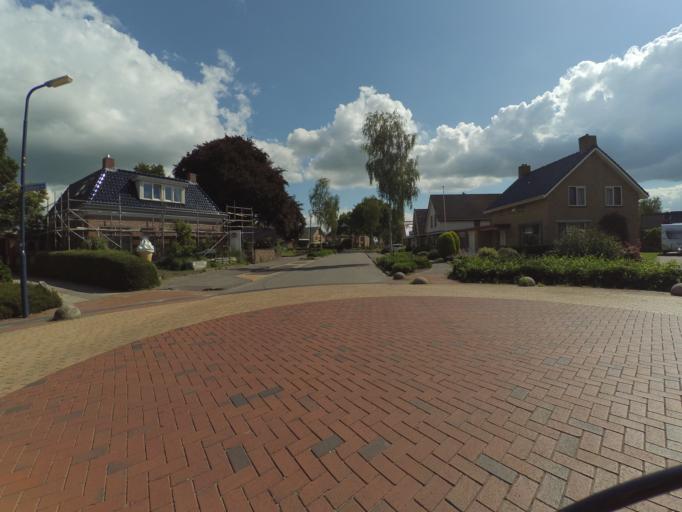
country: NL
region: Friesland
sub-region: Gemeente Achtkarspelen
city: Drogeham
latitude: 53.2028
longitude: 6.1176
